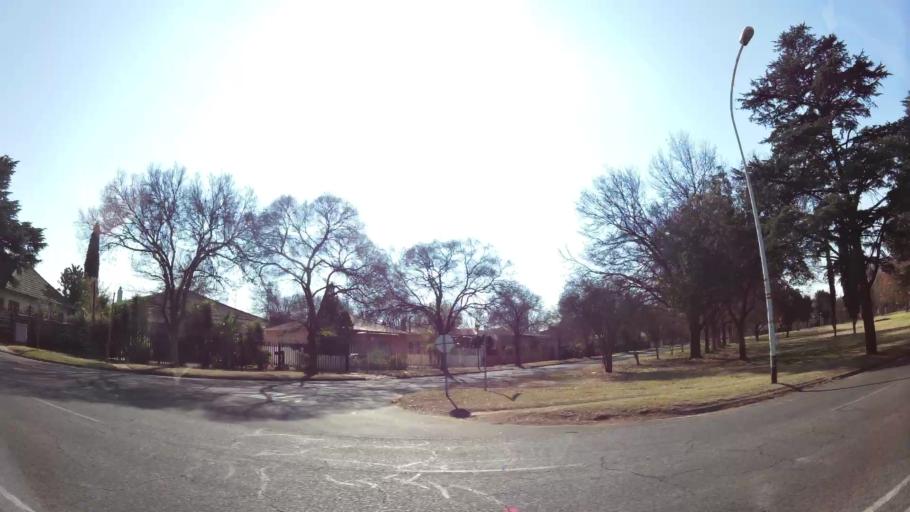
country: ZA
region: Gauteng
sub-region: Ekurhuleni Metropolitan Municipality
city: Boksburg
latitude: -26.2269
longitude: 28.2659
